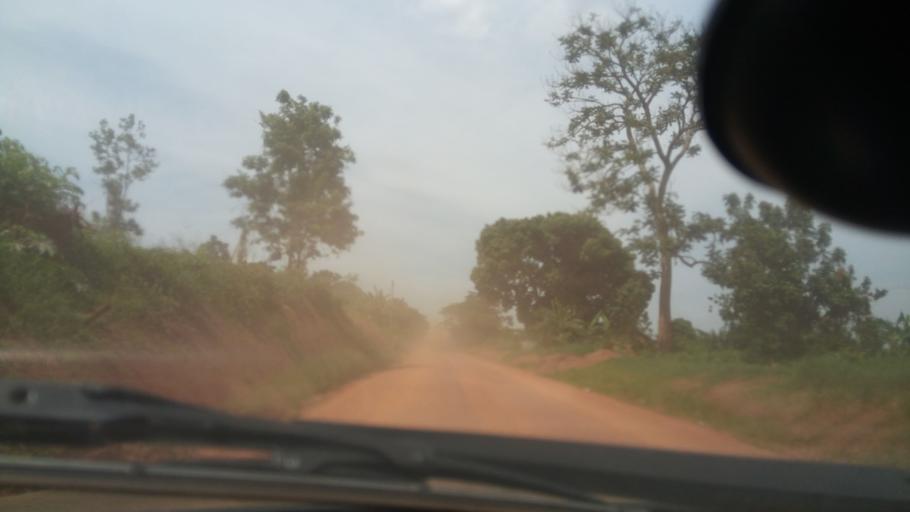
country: UG
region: Central Region
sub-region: Mityana District
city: Mityana
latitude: 0.4981
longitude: 32.1313
